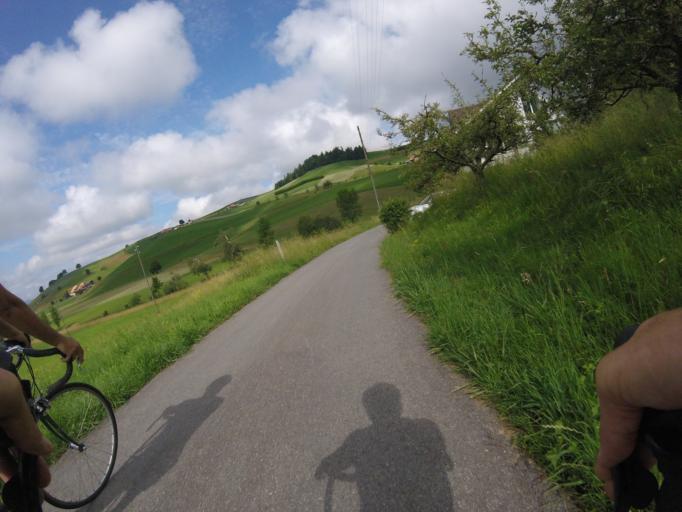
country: CH
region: Bern
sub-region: Bern-Mittelland District
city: Vechigen
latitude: 46.9721
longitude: 7.5827
